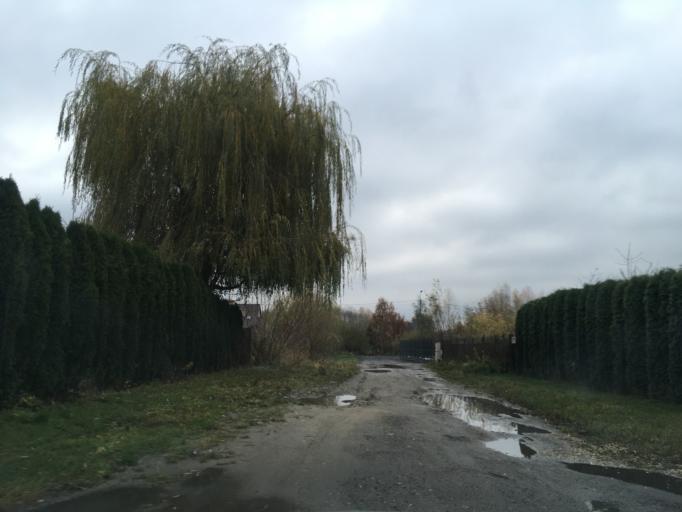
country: PL
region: Masovian Voivodeship
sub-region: Powiat pruszkowski
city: Brwinow
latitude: 52.1426
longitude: 20.7381
